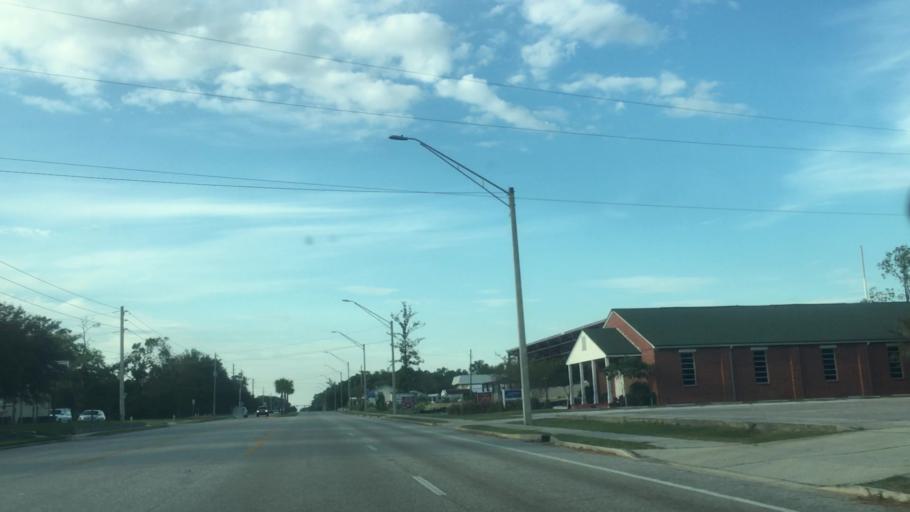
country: US
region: Florida
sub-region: Duval County
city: Atlantic Beach
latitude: 30.3337
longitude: -81.5232
